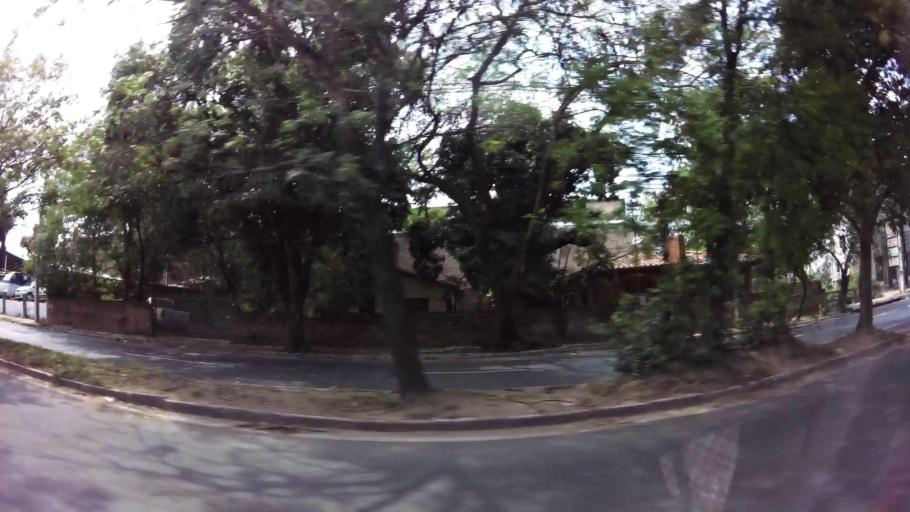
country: PY
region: Asuncion
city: Asuncion
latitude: -25.2626
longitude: -57.5816
